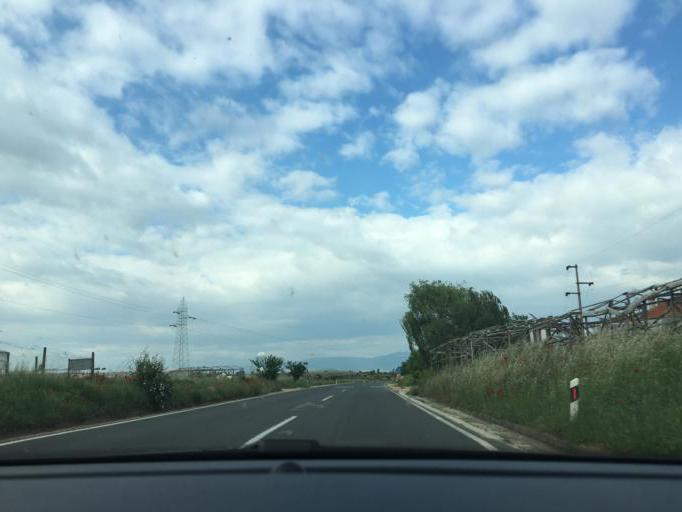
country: MK
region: Prilep
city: Prilep
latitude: 41.3328
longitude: 21.5641
